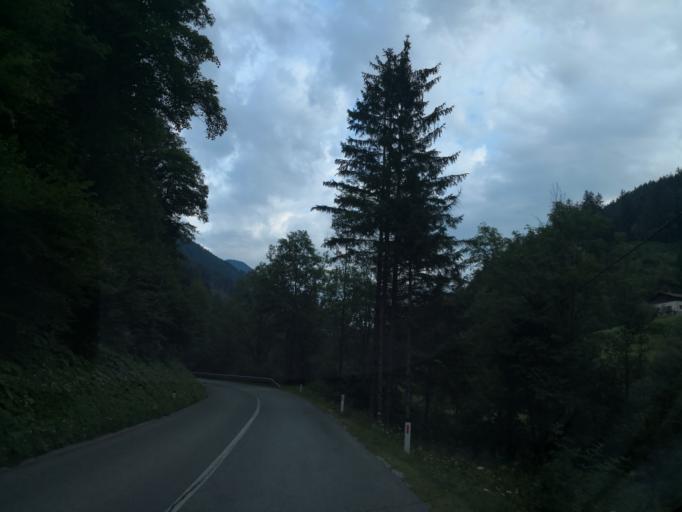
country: SI
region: Jezersko
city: Zgornje Jezersko
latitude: 46.3357
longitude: 14.4917
